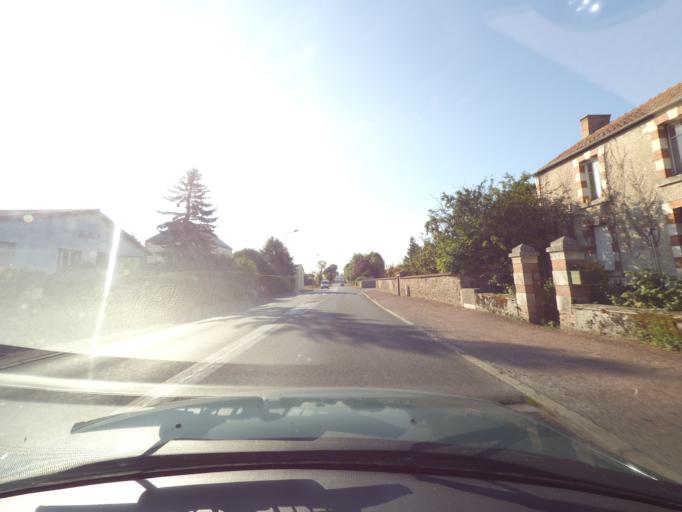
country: FR
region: Poitou-Charentes
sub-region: Departement des Deux-Sevres
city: Boisme
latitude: 46.8233
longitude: -0.4151
